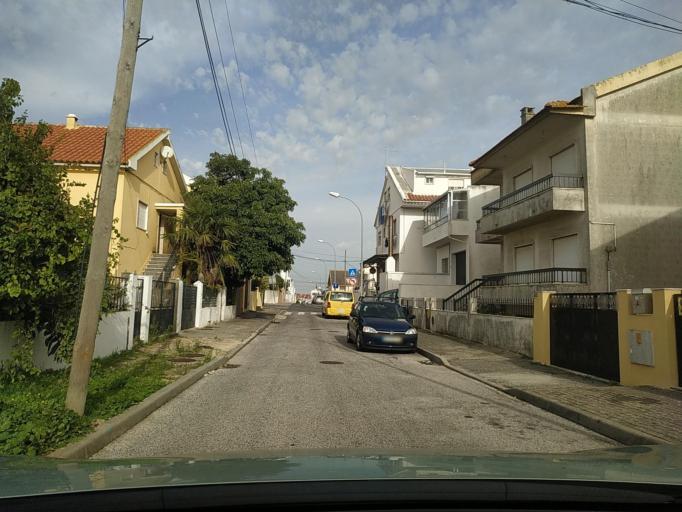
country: PT
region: Lisbon
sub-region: Sintra
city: Belas
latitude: 38.7776
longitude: -9.2437
